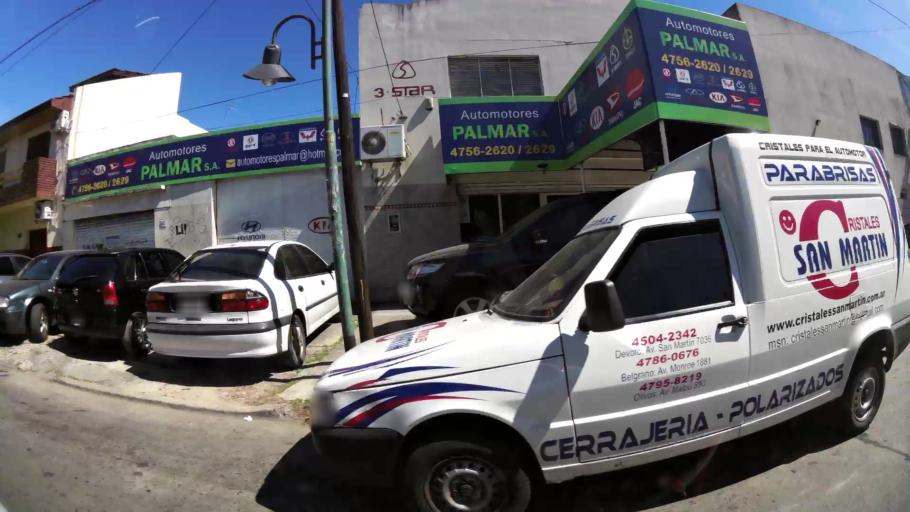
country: AR
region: Buenos Aires
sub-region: Partido de Vicente Lopez
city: Olivos
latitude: -34.5230
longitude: -58.5246
